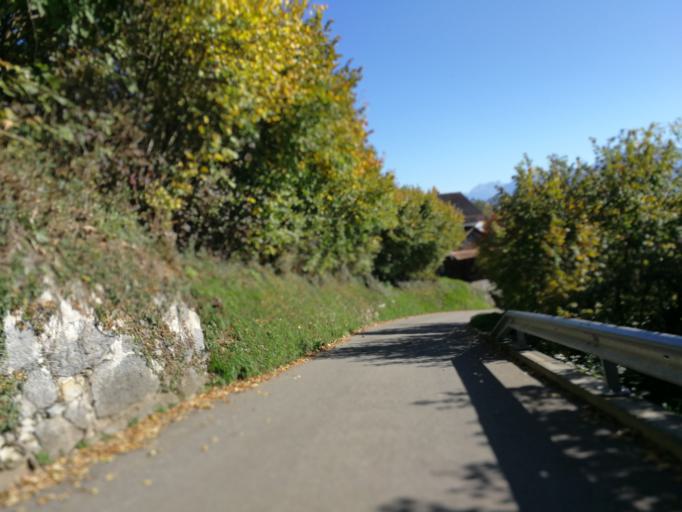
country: CH
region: Zurich
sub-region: Bezirk Hinwil
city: Wolfhausen
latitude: 47.2460
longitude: 8.8003
